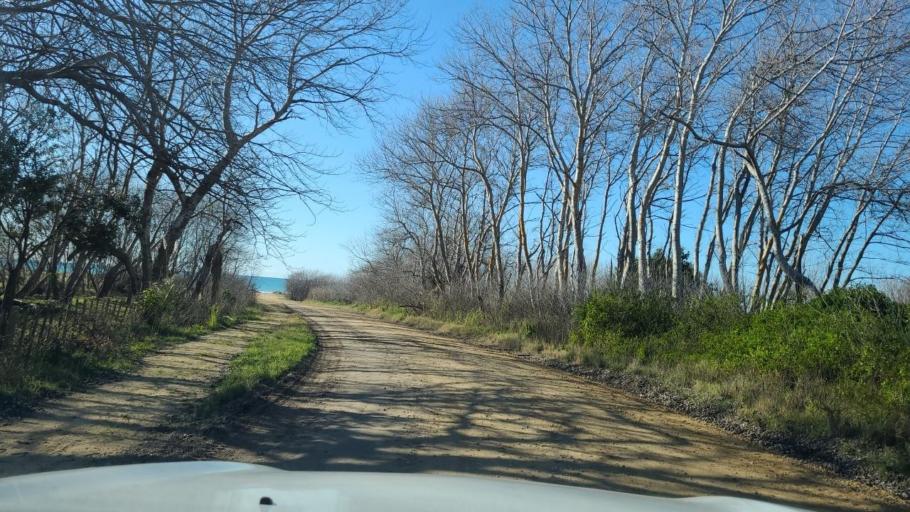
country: NZ
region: Hawke's Bay
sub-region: Hastings District
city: Hastings
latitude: -39.8069
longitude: 176.9912
